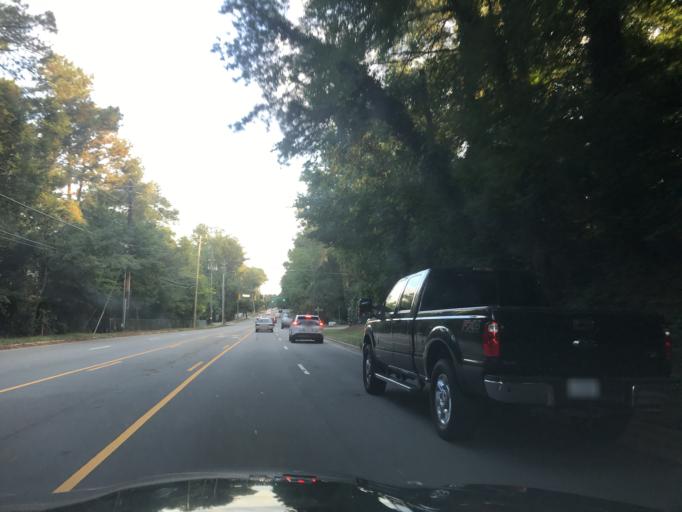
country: US
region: North Carolina
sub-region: Wake County
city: West Raleigh
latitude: 35.8292
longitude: -78.6350
